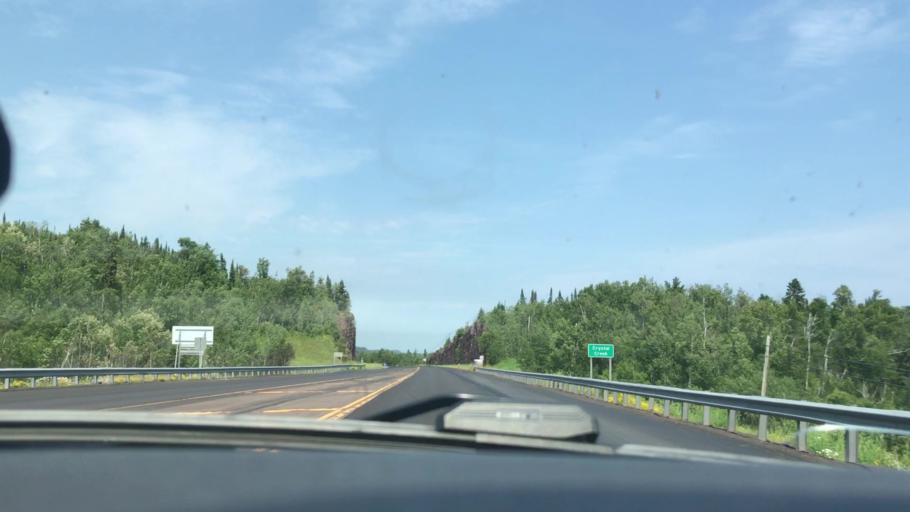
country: US
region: Minnesota
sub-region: Lake County
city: Silver Bay
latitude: 47.3473
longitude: -91.1867
